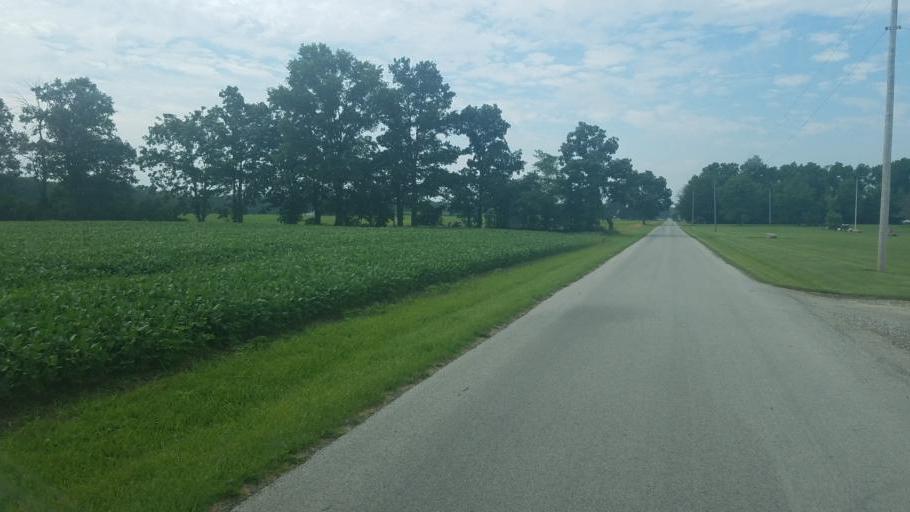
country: US
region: Ohio
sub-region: Morrow County
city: Cardington
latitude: 40.5076
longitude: -82.9487
